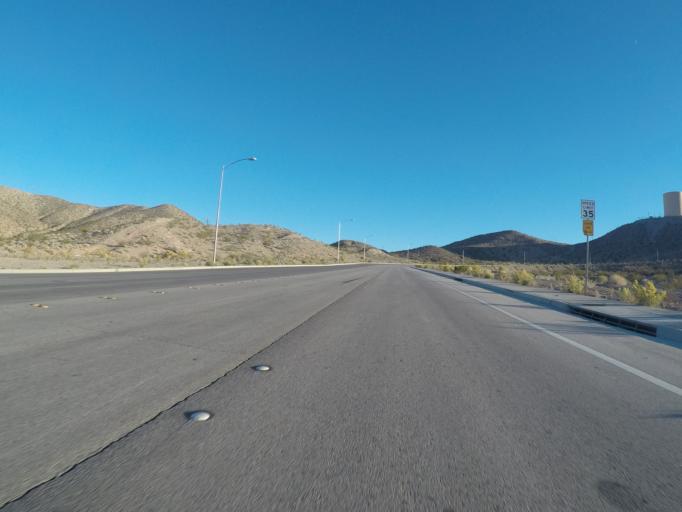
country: US
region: Nevada
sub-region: Clark County
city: Boulder City
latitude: 35.9848
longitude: -114.8289
